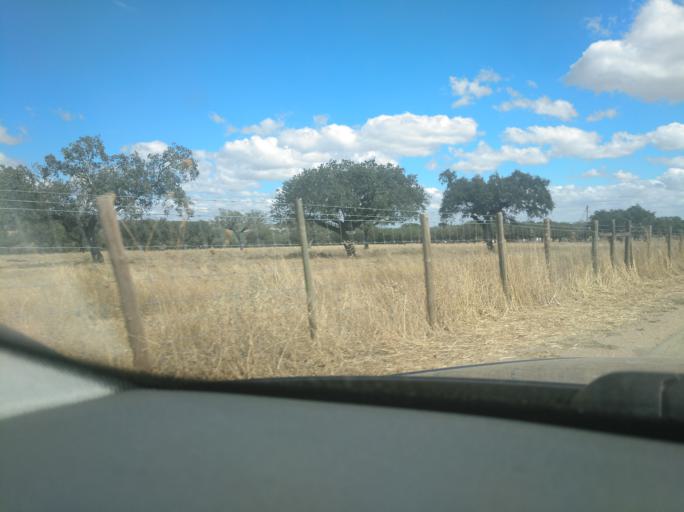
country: ES
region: Extremadura
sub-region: Provincia de Badajoz
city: La Codosera
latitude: 39.1305
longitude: -7.1563
